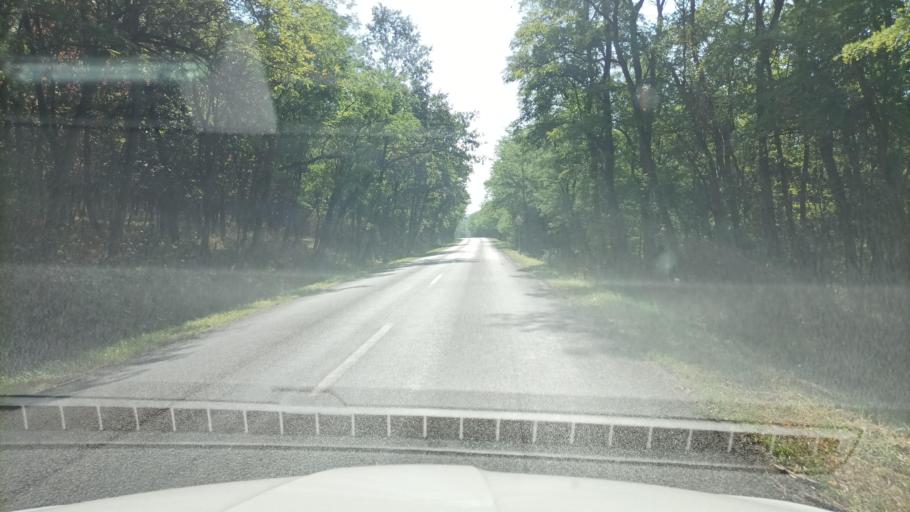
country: HU
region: Pest
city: Isaszeg
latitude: 47.5703
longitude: 19.4417
